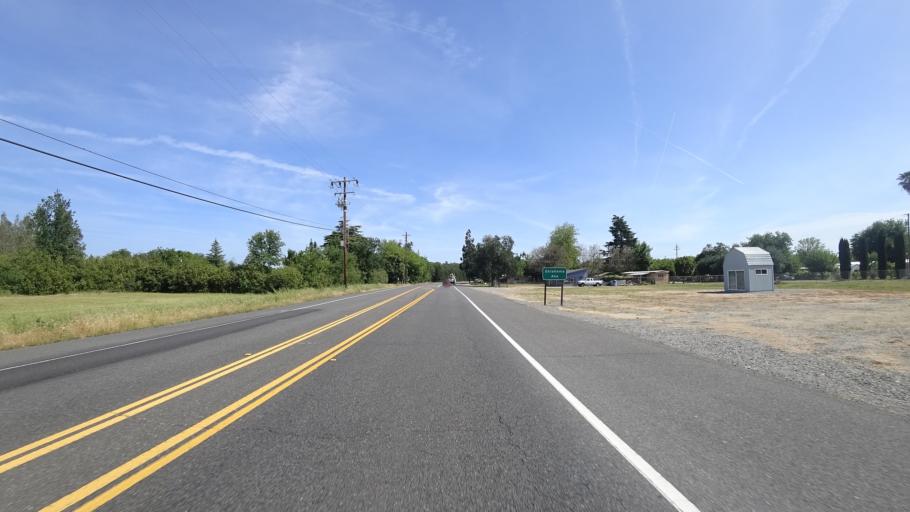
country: US
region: California
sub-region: Tehama County
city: Gerber
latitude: 40.1342
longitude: -122.1253
